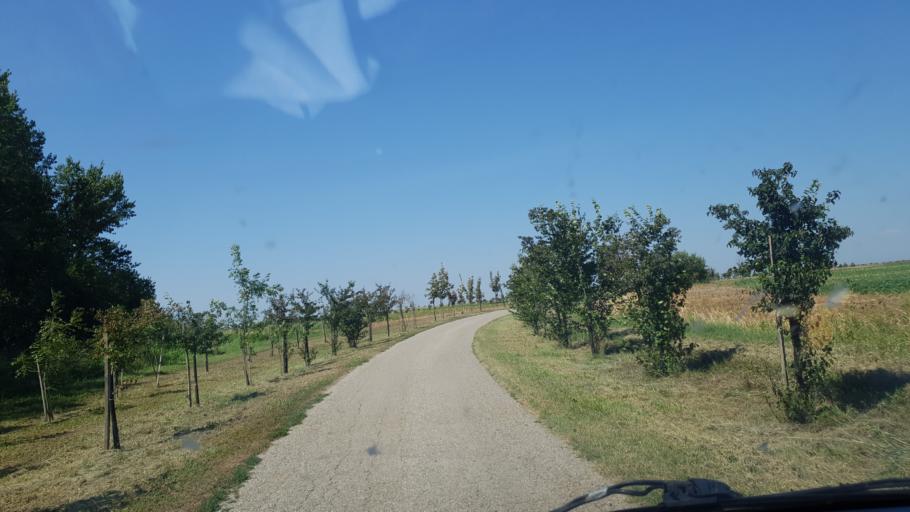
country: RS
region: Autonomna Pokrajina Vojvodina
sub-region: Juznobacki Okrug
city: Kovilj
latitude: 45.2071
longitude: 20.0632
